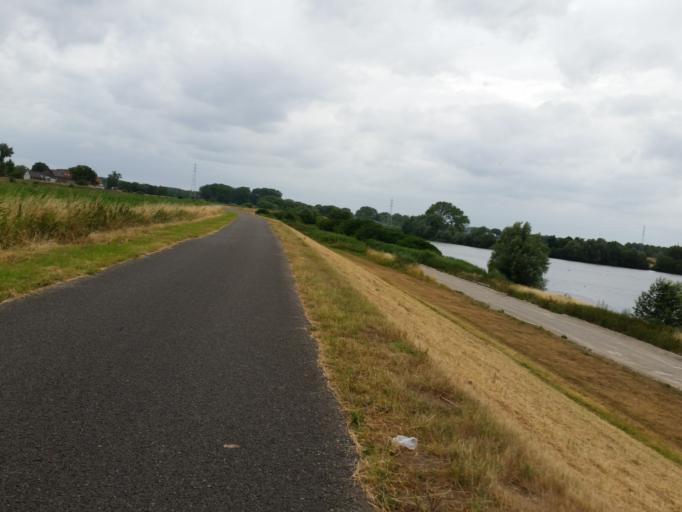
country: BE
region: Flanders
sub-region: Provincie Antwerpen
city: Rumst
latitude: 51.0628
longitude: 4.4363
